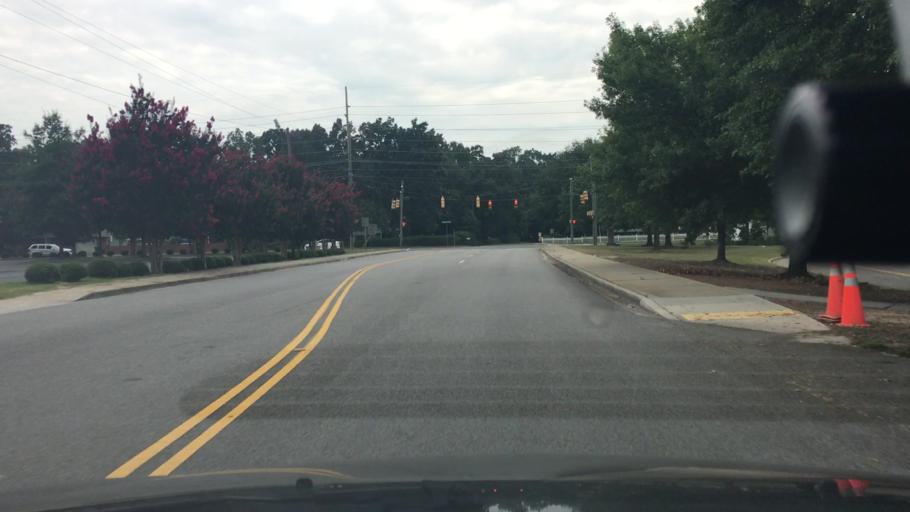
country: US
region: South Carolina
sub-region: Aiken County
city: Aiken
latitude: 33.5242
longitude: -81.7152
